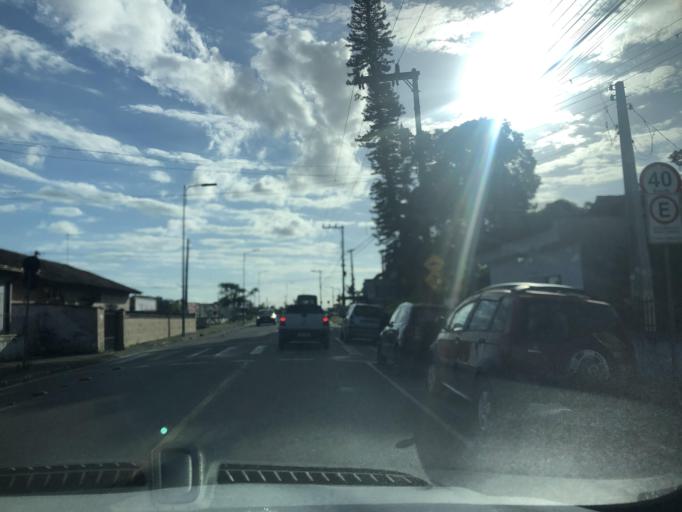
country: BR
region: Santa Catarina
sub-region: Sao Francisco Do Sul
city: Sao Francisco do Sul
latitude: -26.2477
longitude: -48.6368
